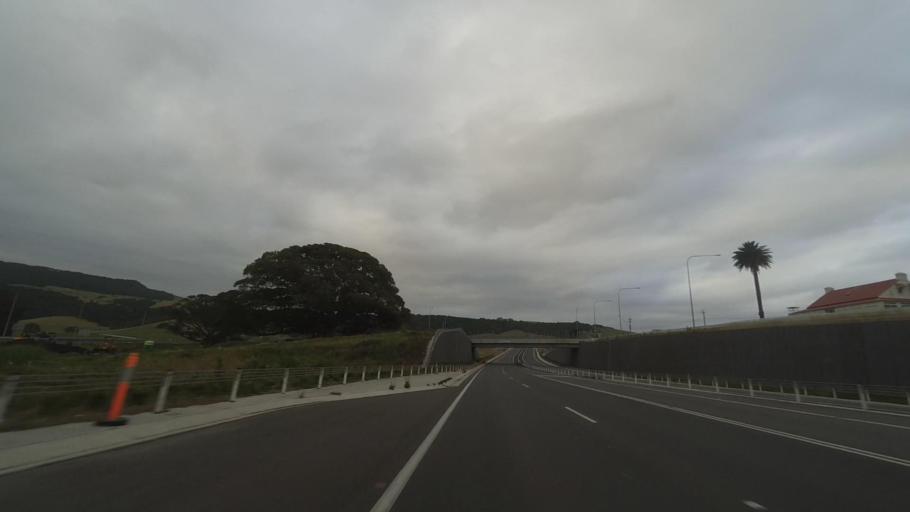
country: AU
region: New South Wales
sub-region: Kiama
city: Gerringong
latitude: -34.7239
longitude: 150.8290
